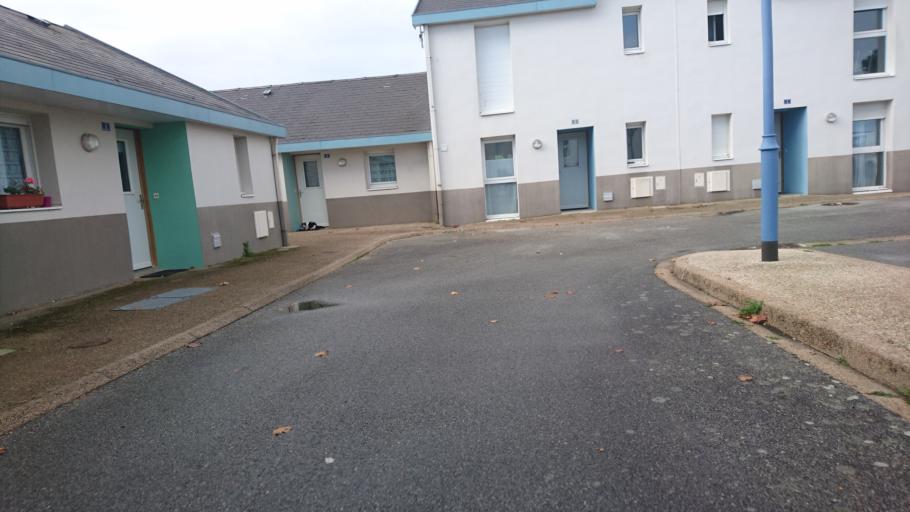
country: FR
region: Brittany
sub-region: Departement du Finistere
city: Lampaul-Plouarzel
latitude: 48.4468
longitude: -4.7592
